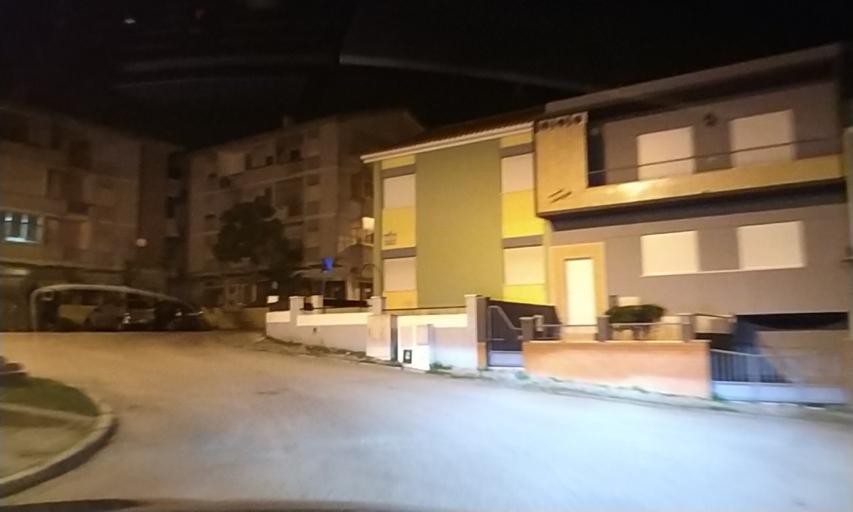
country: PT
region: Setubal
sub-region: Setubal
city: Setubal
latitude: 38.5299
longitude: -8.9052
